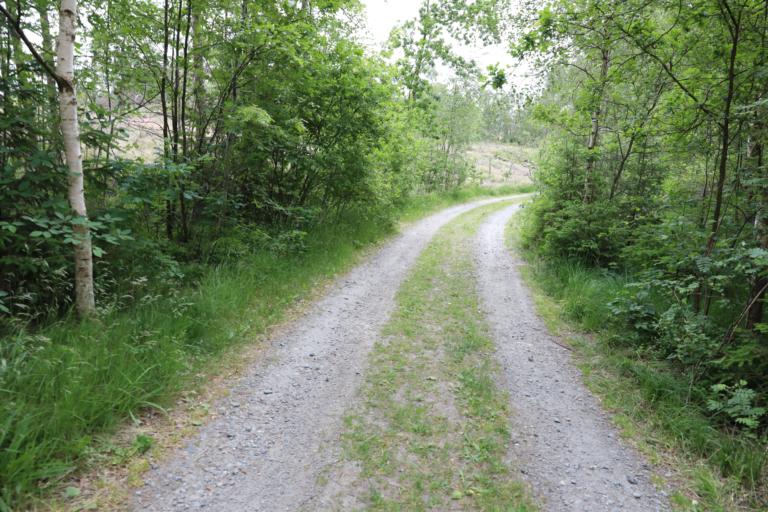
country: SE
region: Halland
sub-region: Varbergs Kommun
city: Varberg
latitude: 57.1688
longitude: 12.2608
